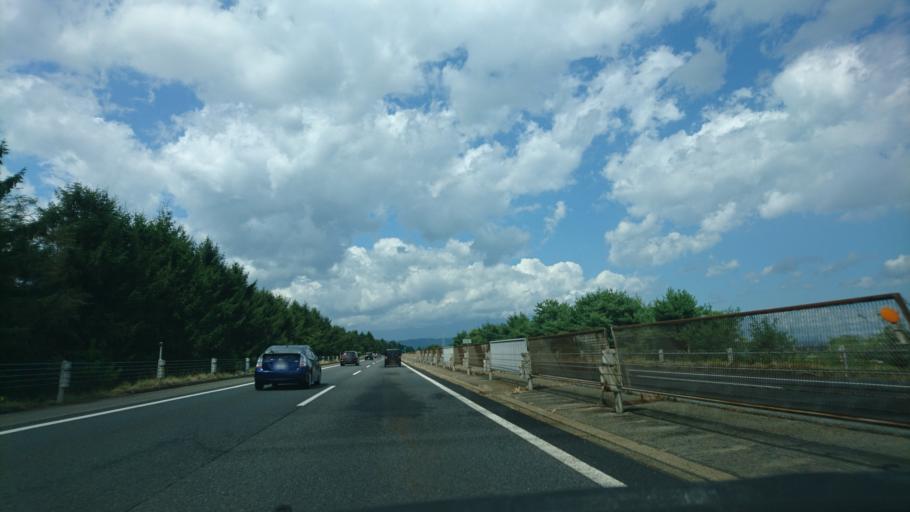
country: JP
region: Iwate
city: Morioka-shi
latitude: 39.6663
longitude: 141.1117
